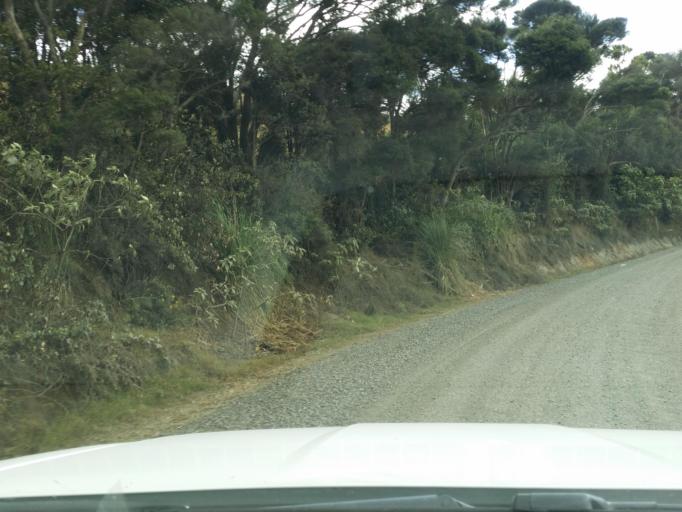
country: NZ
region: Auckland
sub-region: Auckland
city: Wellsford
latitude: -36.3167
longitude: 174.1346
